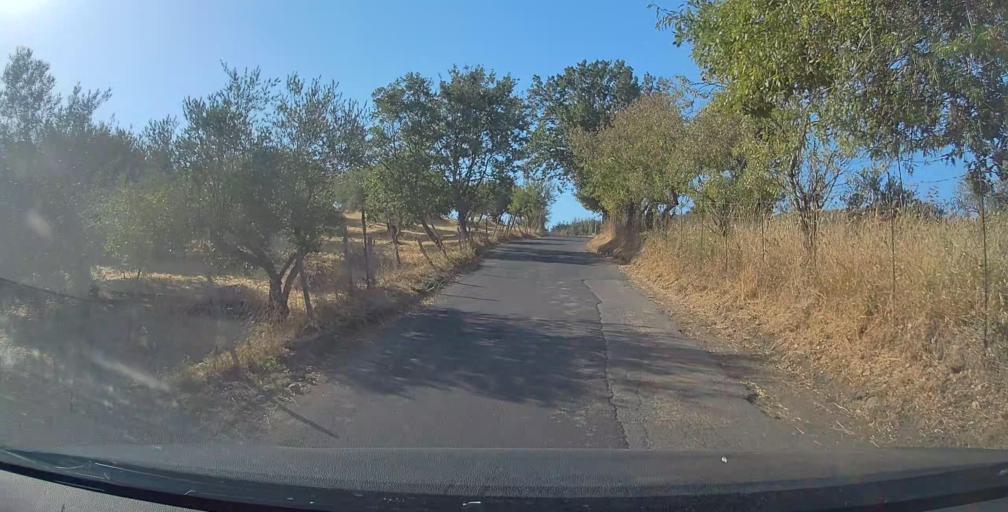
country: IT
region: Sicily
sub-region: Messina
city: San Piero Patti
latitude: 38.0622
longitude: 14.9895
